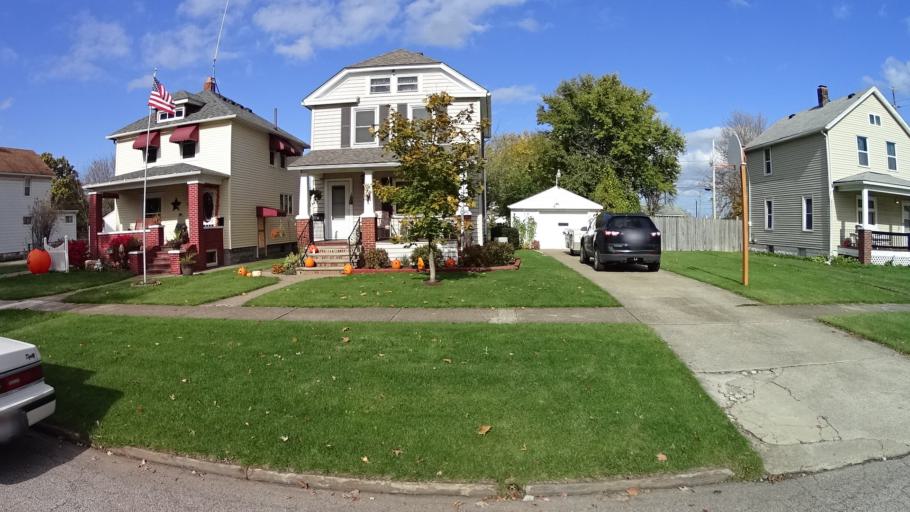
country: US
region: Ohio
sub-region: Lorain County
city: Sheffield
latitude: 41.4438
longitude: -82.1109
